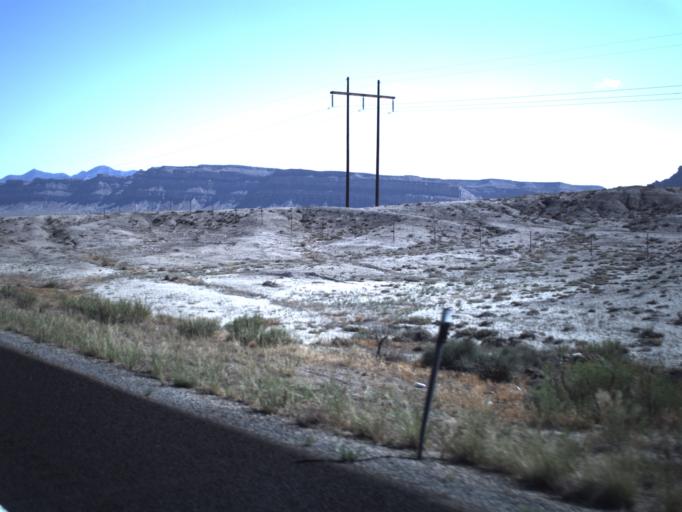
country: US
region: Utah
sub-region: Carbon County
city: East Carbon City
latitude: 39.2115
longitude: -110.3386
